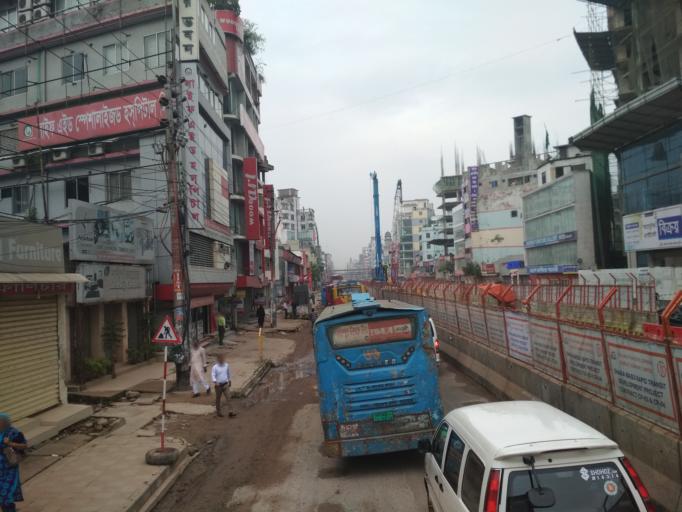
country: BD
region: Dhaka
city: Azimpur
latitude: 23.8005
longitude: 90.3715
